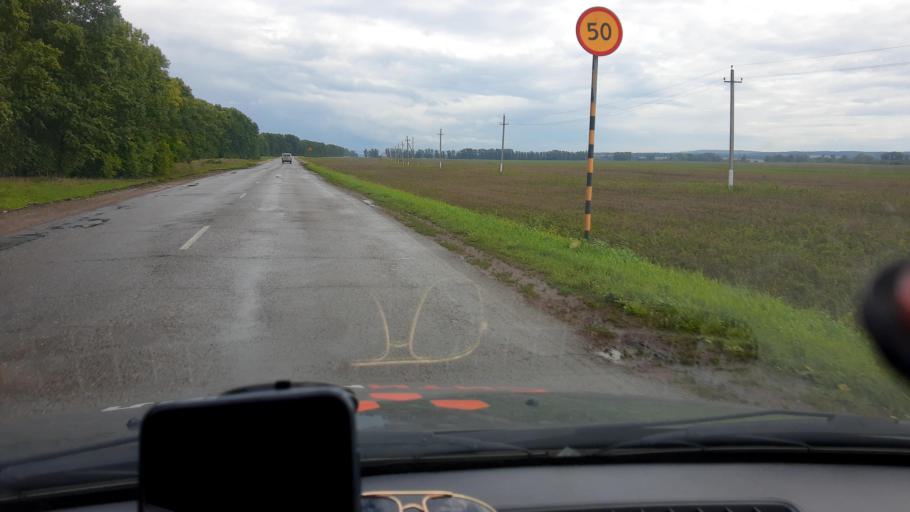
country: RU
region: Bashkortostan
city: Karmaskaly
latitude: 53.9732
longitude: 56.3898
